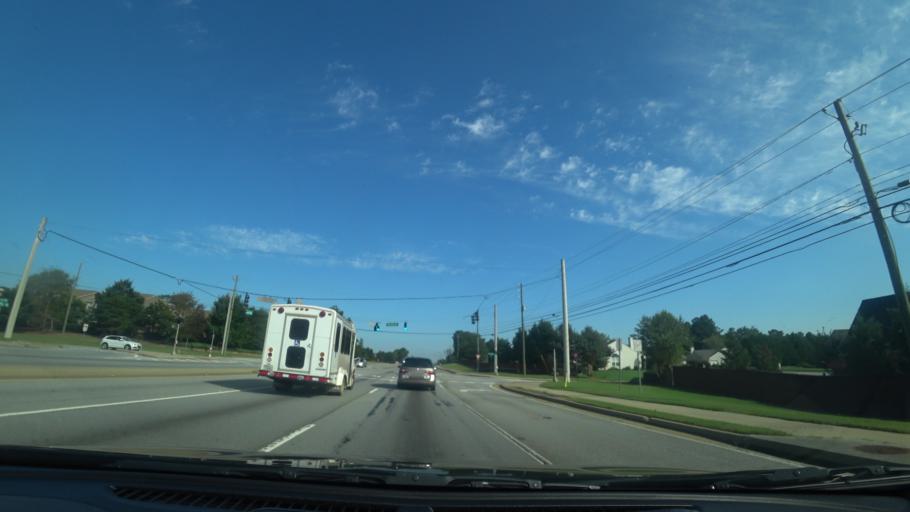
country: US
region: Georgia
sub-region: Gwinnett County
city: Grayson
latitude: 33.9065
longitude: -83.9665
